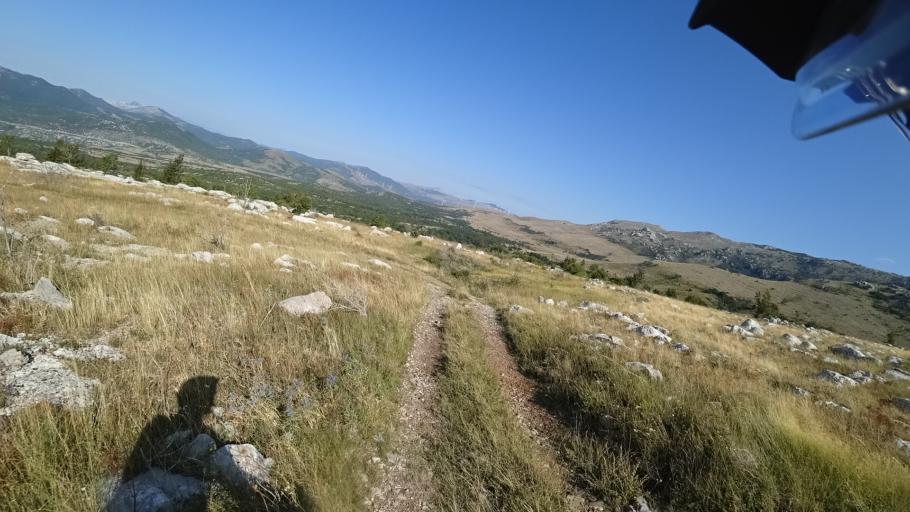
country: HR
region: Sibensko-Kniniska
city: Knin
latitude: 44.2127
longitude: 16.1136
